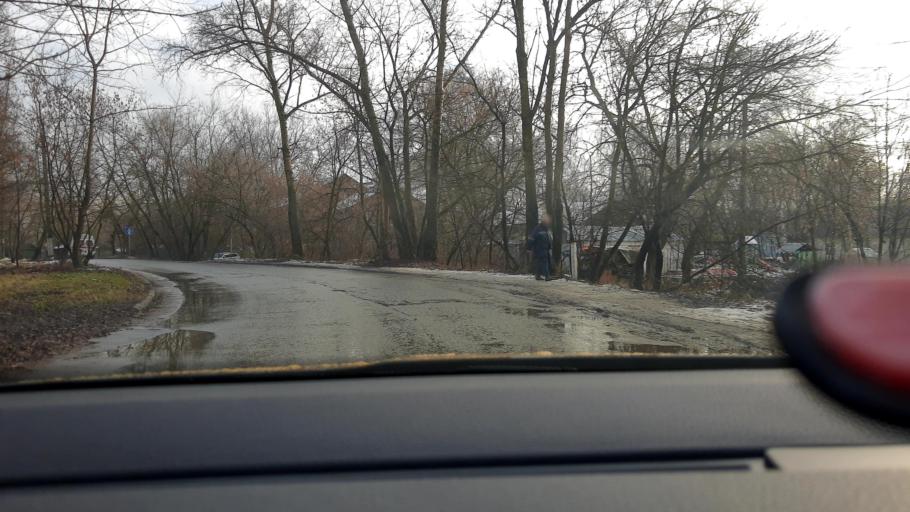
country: RU
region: Moskovskaya
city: Pushkino
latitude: 55.9930
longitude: 37.8607
